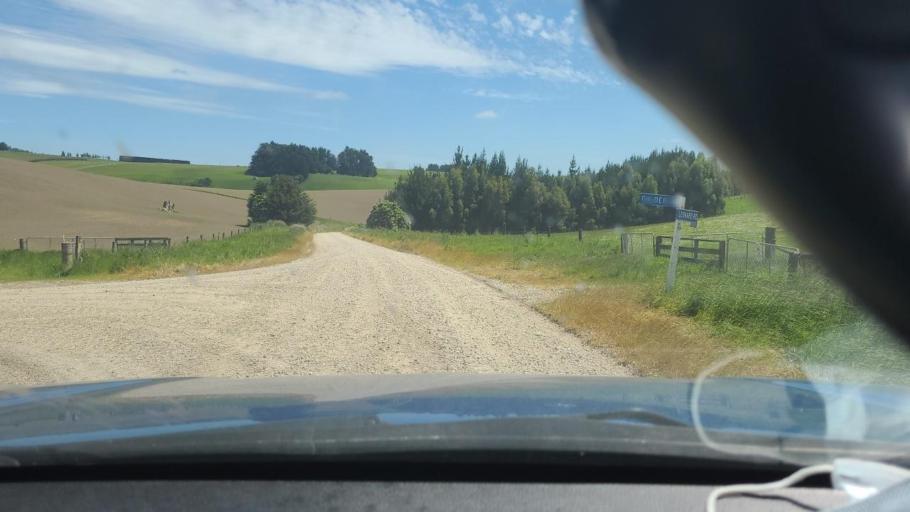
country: NZ
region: Southland
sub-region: Gore District
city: Gore
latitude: -46.3728
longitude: 168.8841
